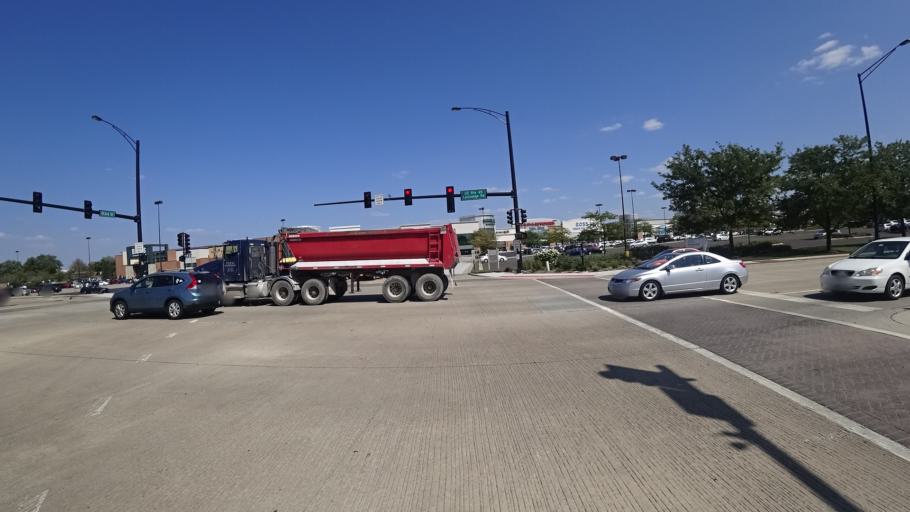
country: US
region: Illinois
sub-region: Cook County
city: Orland Park
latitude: 41.6121
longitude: -87.8533
